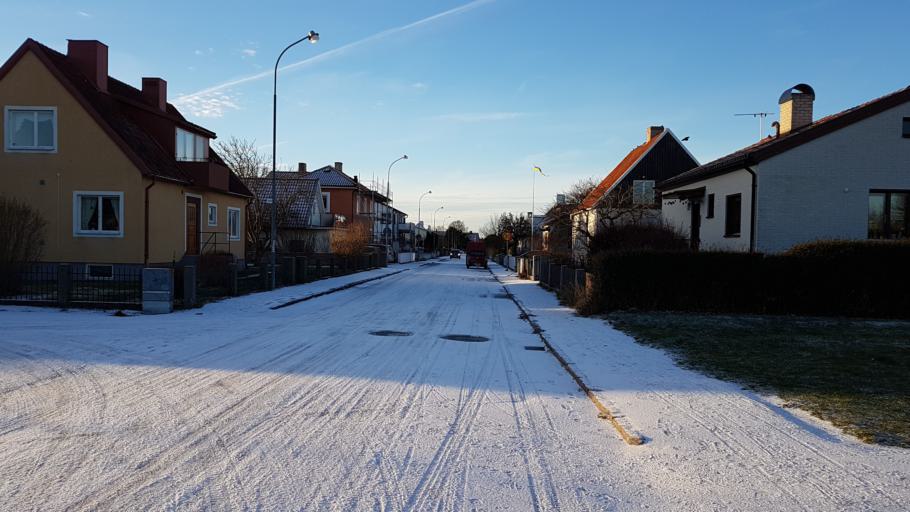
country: SE
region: Gotland
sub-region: Gotland
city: Visby
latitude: 57.6411
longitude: 18.3063
